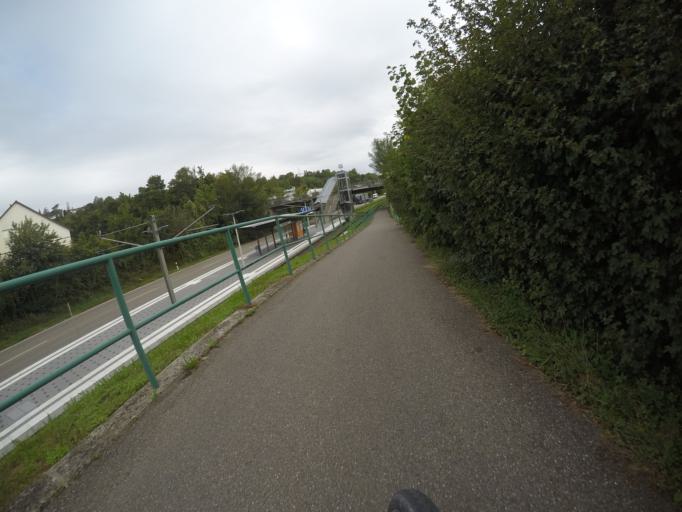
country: DE
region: Baden-Wuerttemberg
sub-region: Regierungsbezirk Stuttgart
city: Stuttgart Muehlhausen
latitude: 48.8665
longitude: 9.2579
